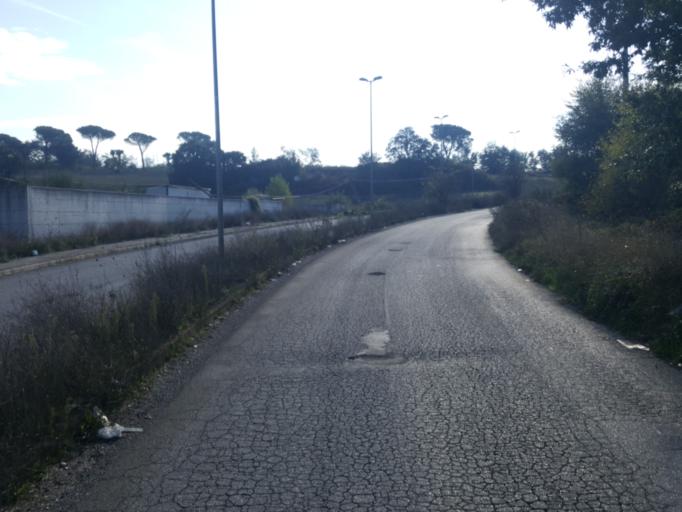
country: IT
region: Latium
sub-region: Citta metropolitana di Roma Capitale
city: Colleferro
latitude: 41.7577
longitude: 13.0003
